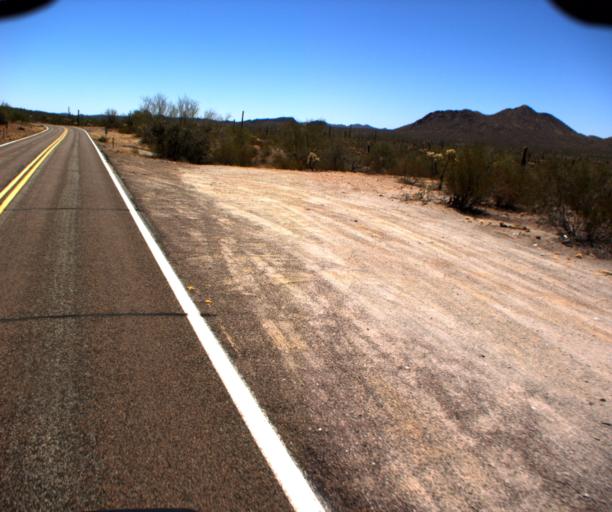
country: US
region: Arizona
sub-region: Pima County
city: Ajo
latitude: 32.2232
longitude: -112.6992
